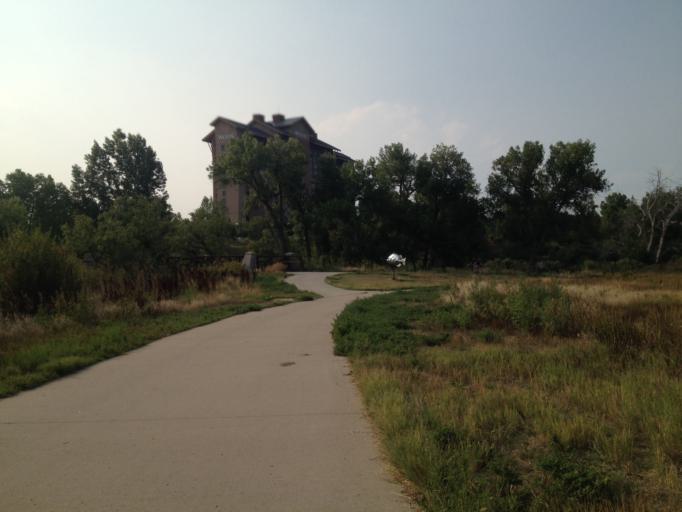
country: US
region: Colorado
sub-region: Broomfield County
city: Broomfield
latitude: 39.8885
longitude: -105.0641
